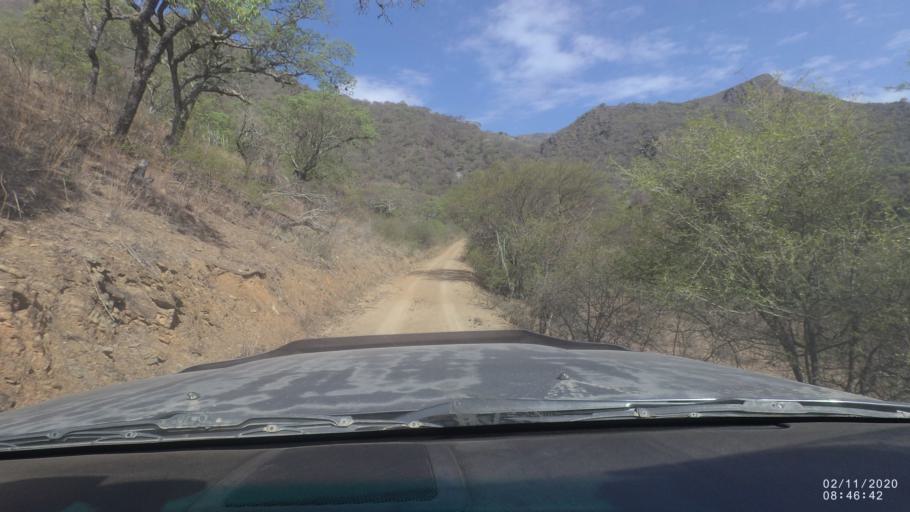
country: BO
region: Chuquisaca
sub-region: Provincia Zudanez
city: Mojocoya
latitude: -18.5632
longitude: -64.5460
